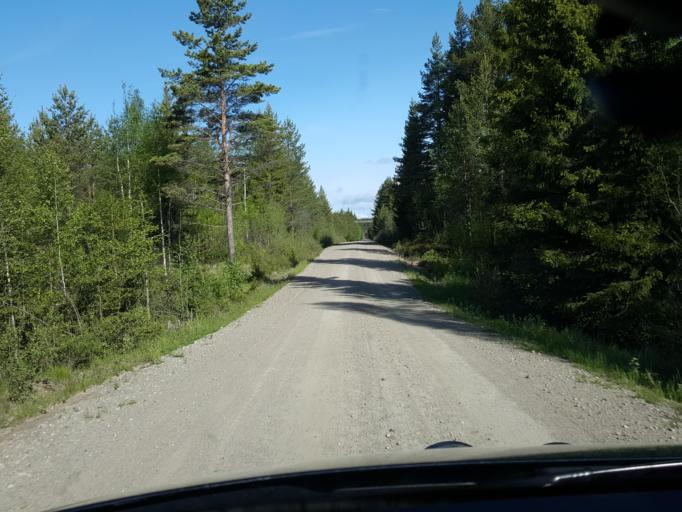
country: SE
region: Vaesternorrland
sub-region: Ange Kommun
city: Ange
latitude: 62.1858
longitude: 15.6049
